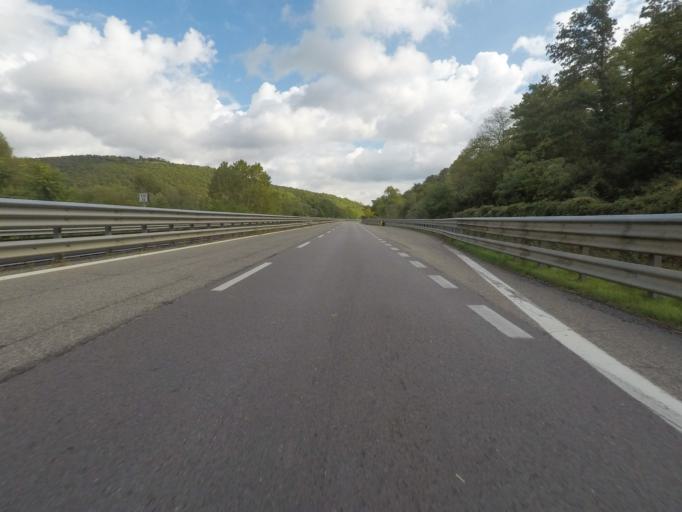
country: IT
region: Tuscany
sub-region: Provincia di Siena
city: Serre di Rapolano
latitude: 43.2506
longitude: 11.6717
